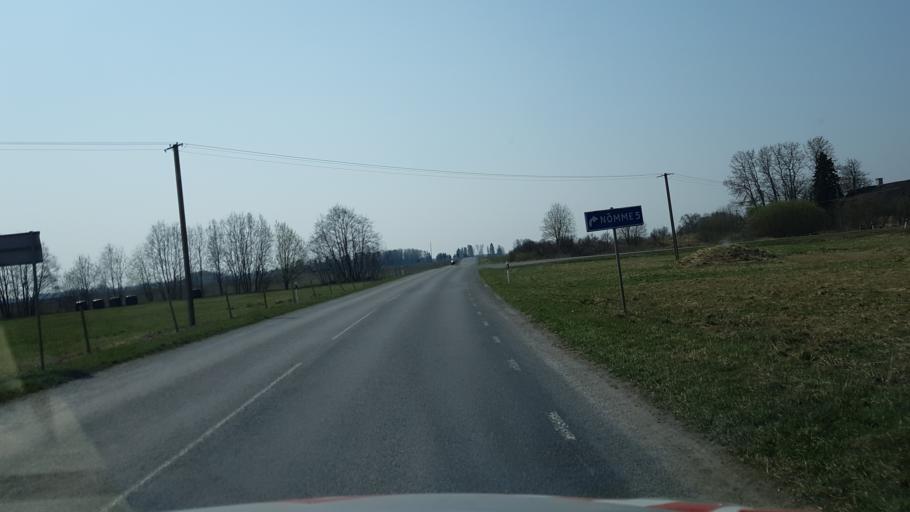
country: EE
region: Raplamaa
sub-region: Kehtna vald
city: Kehtna
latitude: 59.0214
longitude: 24.9267
